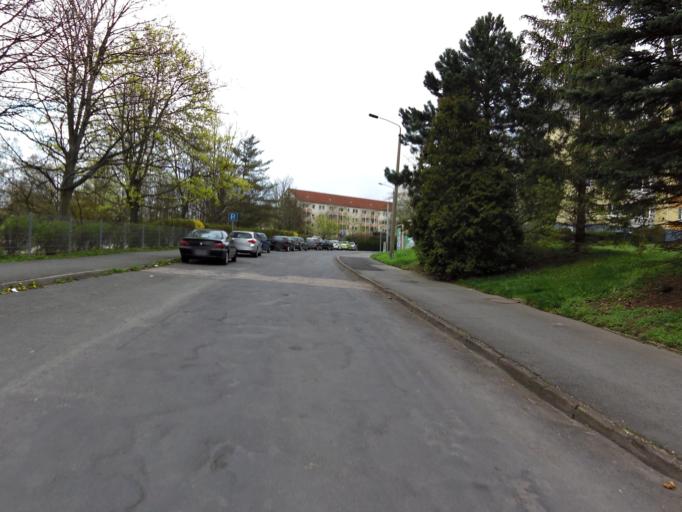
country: DE
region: Thuringia
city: Gotha
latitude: 50.9486
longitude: 10.6839
